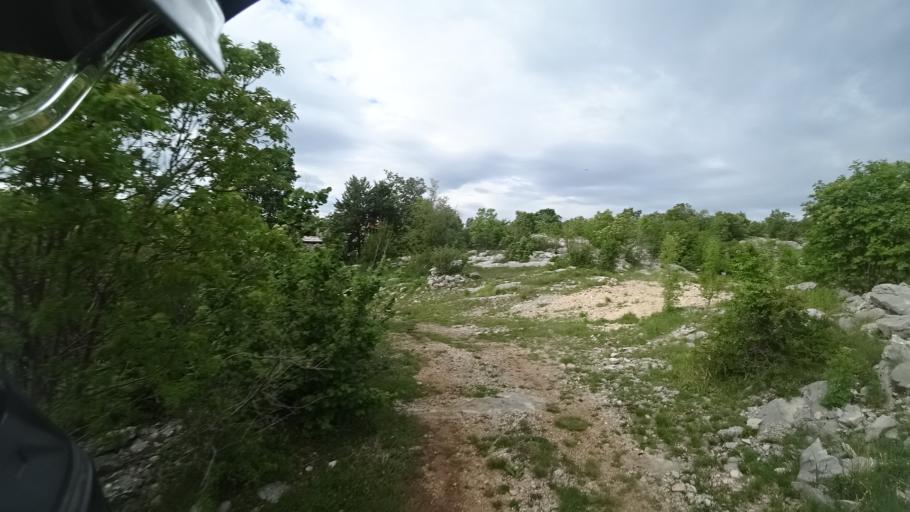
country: HR
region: Sibensko-Kniniska
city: Drnis
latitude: 43.8627
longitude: 16.3931
